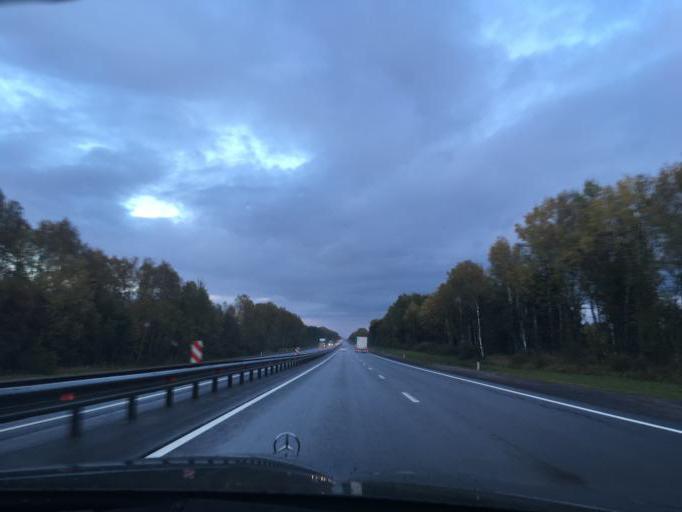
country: RU
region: Smolensk
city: Yartsevo
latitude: 55.1062
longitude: 32.9405
